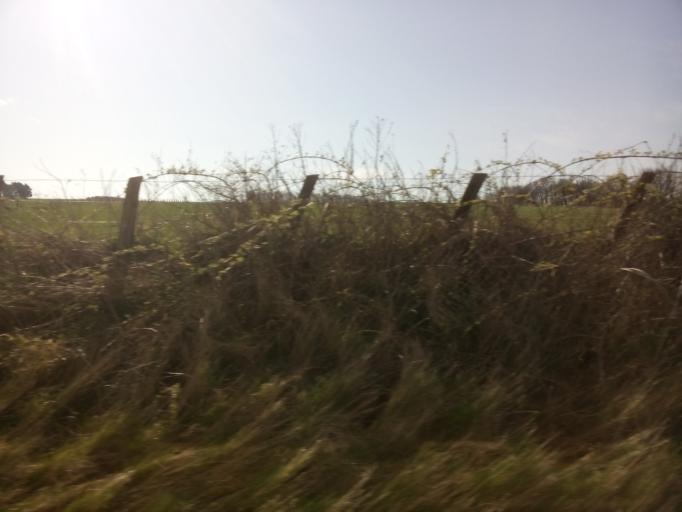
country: GB
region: Scotland
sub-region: East Lothian
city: Longniddry
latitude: 55.9840
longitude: -2.8547
